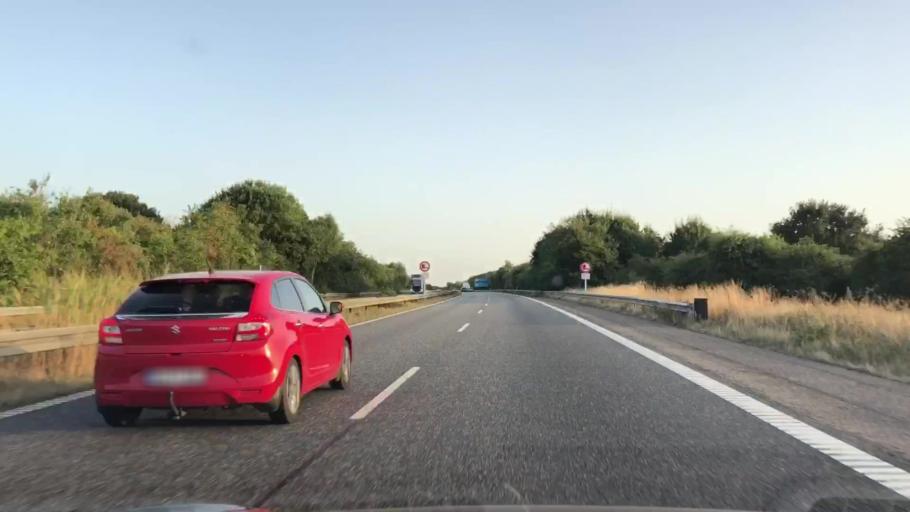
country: DK
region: South Denmark
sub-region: Haderslev Kommune
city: Vojens
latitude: 55.1898
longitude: 9.3709
